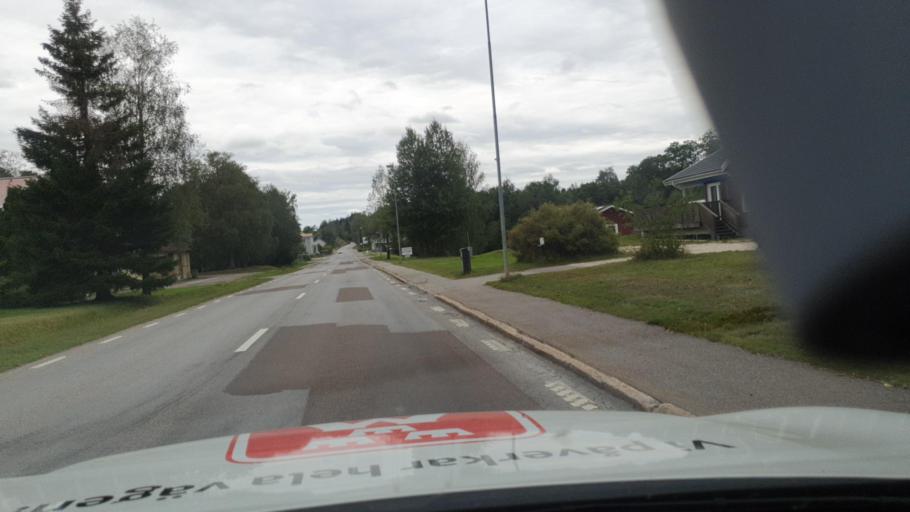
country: SE
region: Vaestra Goetaland
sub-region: Melleruds Kommun
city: Mellerud
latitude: 58.7480
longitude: 12.2923
